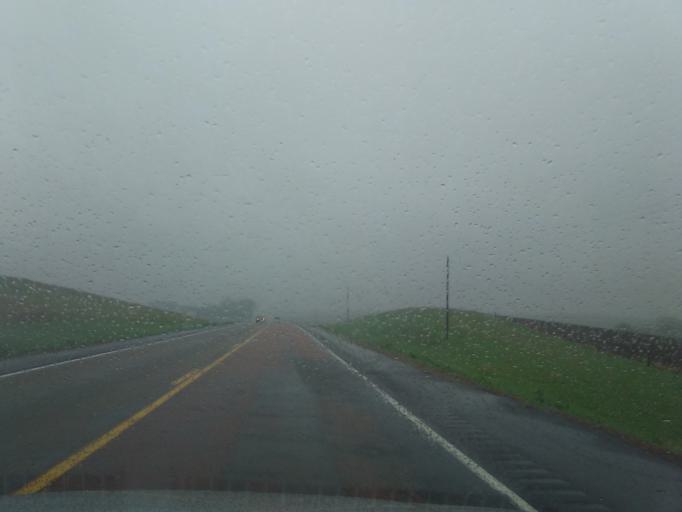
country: US
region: Nebraska
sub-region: Wayne County
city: Wayne
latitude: 42.2356
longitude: -97.0968
